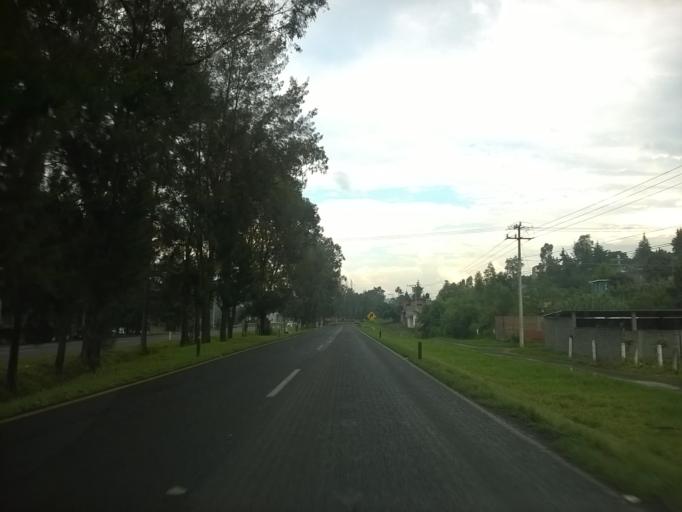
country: MX
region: Michoacan
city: Cuanajo
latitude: 19.5376
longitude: -101.5292
